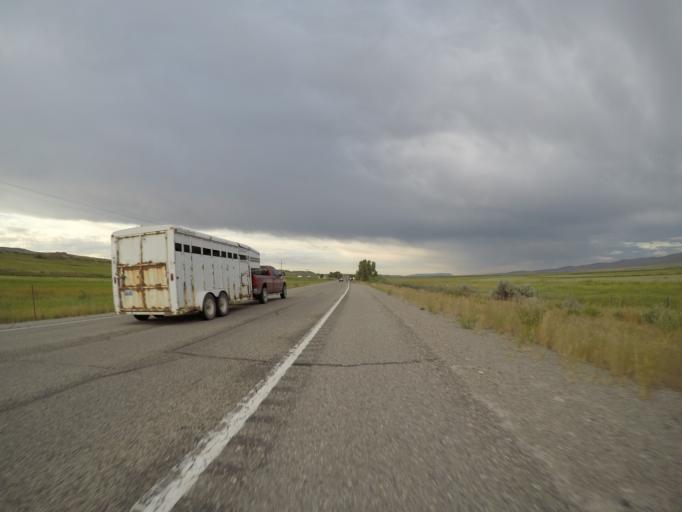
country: US
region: Utah
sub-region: Rich County
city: Randolph
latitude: 42.0337
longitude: -110.9326
